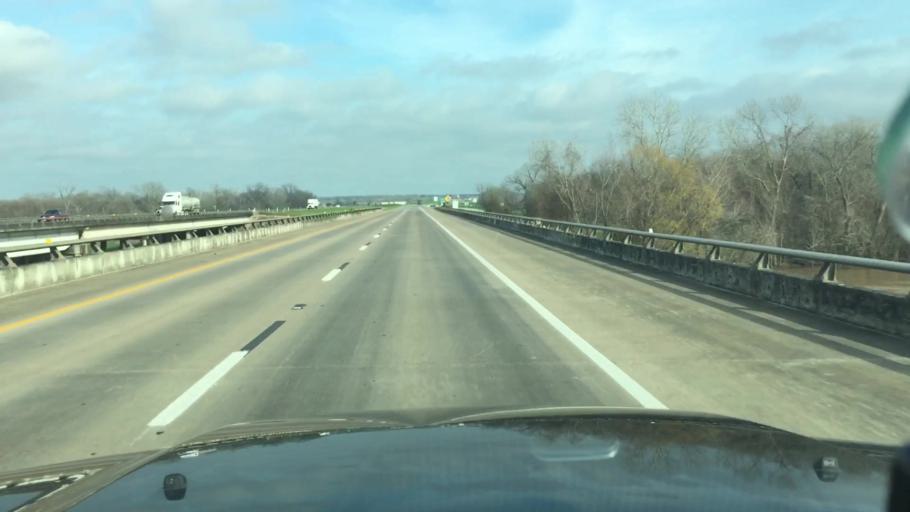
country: US
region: Texas
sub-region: Waller County
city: Hempstead
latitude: 30.1291
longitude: -96.1871
